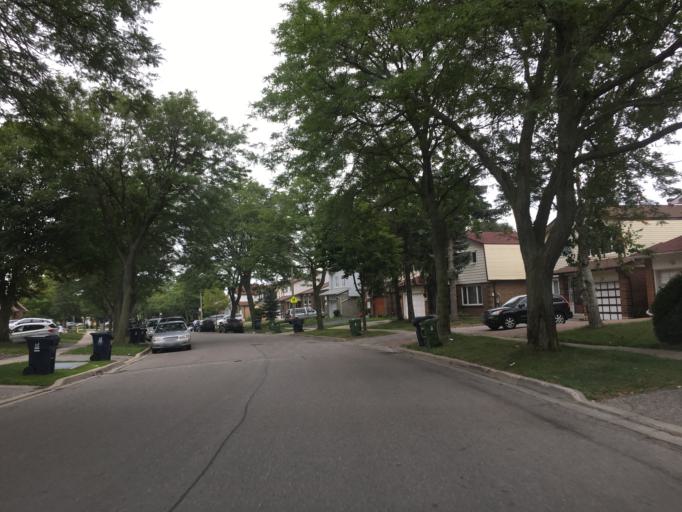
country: CA
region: Ontario
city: Scarborough
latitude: 43.8101
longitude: -79.2872
